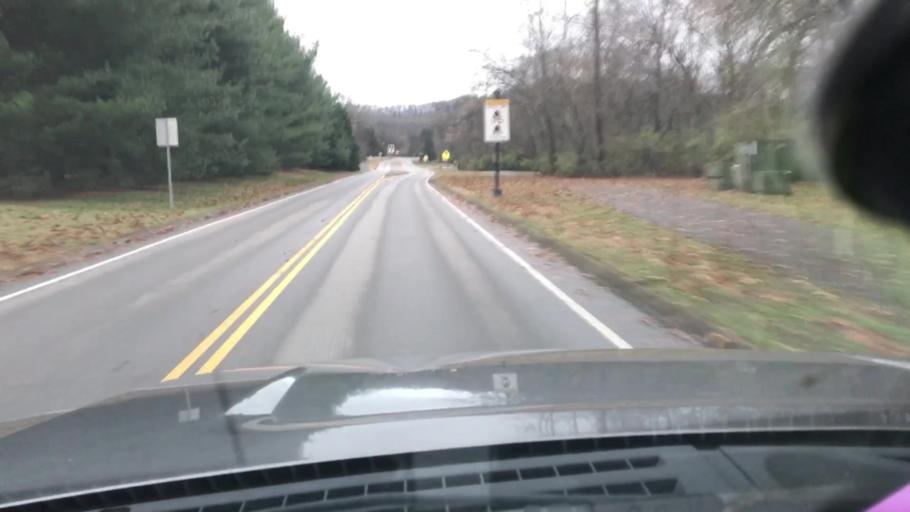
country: US
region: Tennessee
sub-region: Williamson County
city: Brentwood Estates
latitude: 35.9612
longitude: -86.7613
